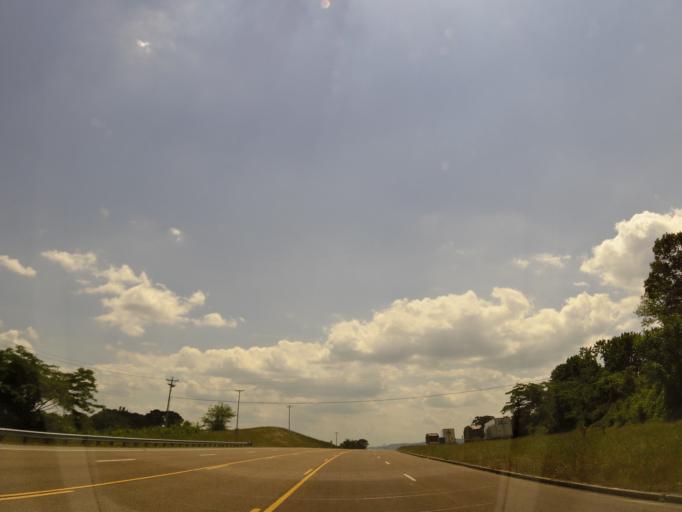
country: US
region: Tennessee
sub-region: Bledsoe County
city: Pikeville
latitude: 35.5946
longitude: -85.1979
